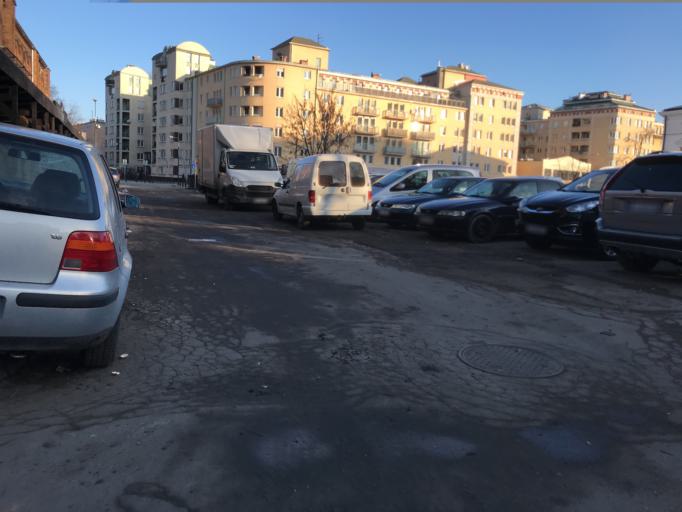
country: PL
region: Masovian Voivodeship
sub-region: Warszawa
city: Wola
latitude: 52.2390
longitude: 21.0004
